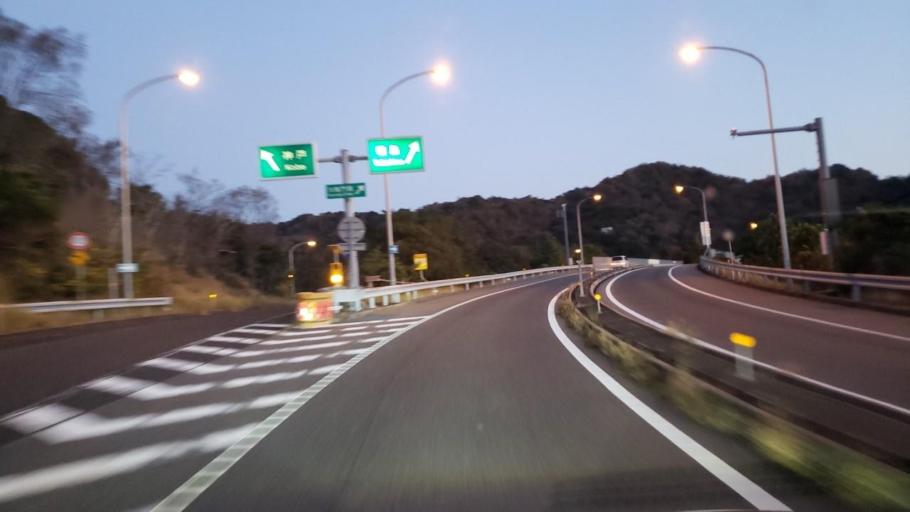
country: JP
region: Hyogo
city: Fukura
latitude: 34.2607
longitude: 134.6831
